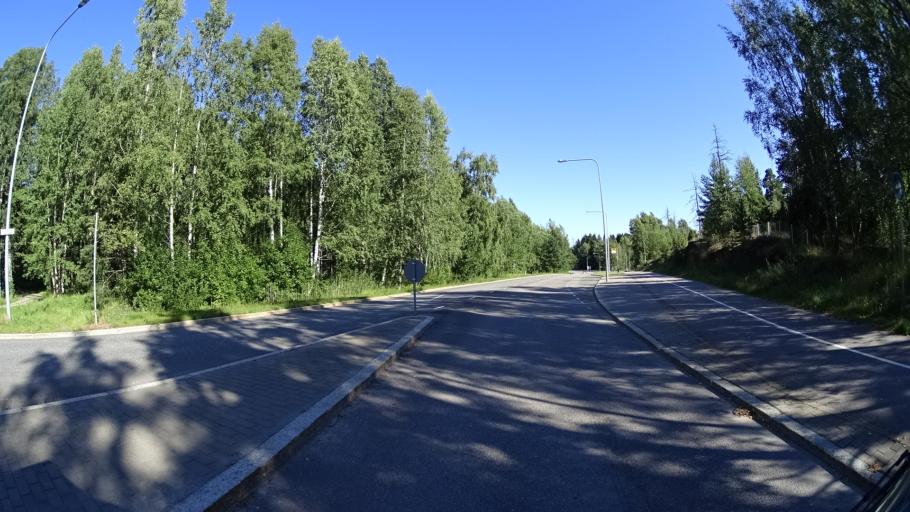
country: FI
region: Uusimaa
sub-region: Helsinki
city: Vantaa
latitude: 60.2225
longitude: 25.1499
